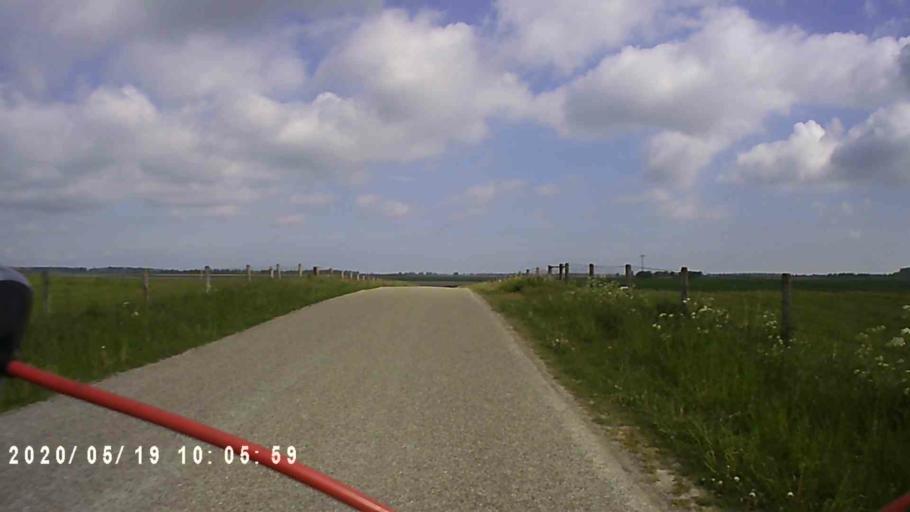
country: NL
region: Friesland
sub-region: Gemeente Kollumerland en Nieuwkruisland
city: Kollum
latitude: 53.3110
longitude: 6.2276
